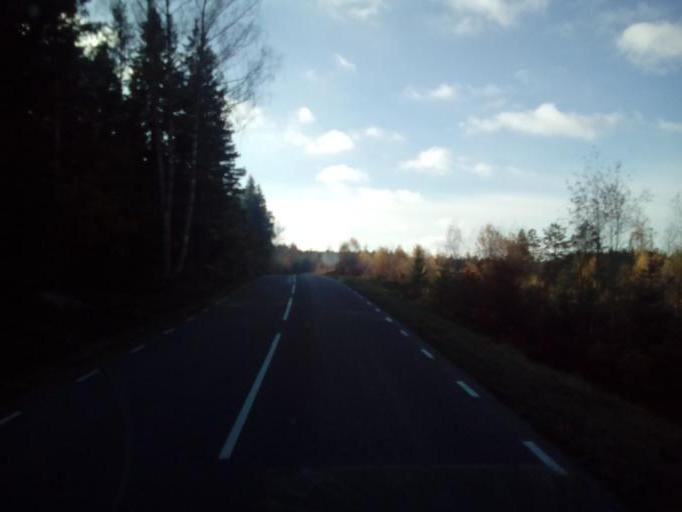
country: SE
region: Kalmar
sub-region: Vasterviks Kommun
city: Ankarsrum
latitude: 57.7427
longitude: 16.1094
